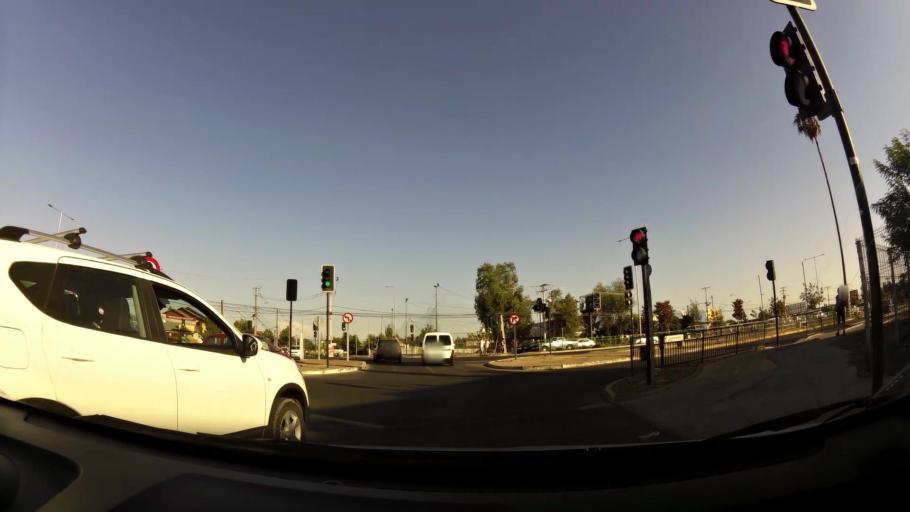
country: CL
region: Maule
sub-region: Provincia de Talca
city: Talca
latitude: -35.4437
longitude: -71.6867
